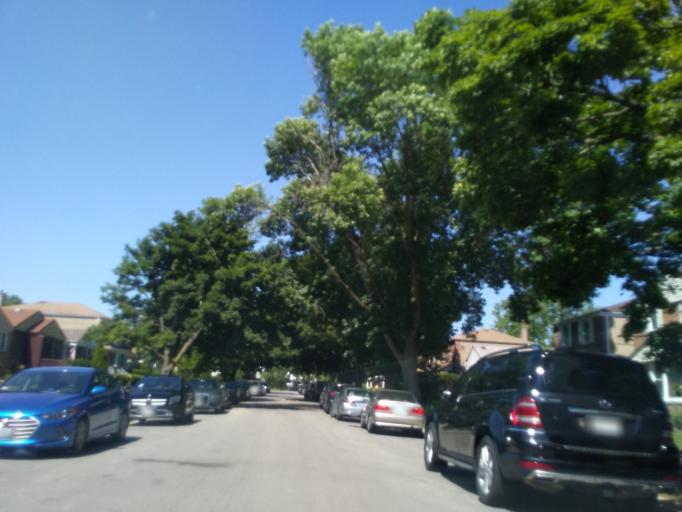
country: US
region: Illinois
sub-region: Cook County
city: Lincolnwood
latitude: 42.0174
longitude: -87.7069
